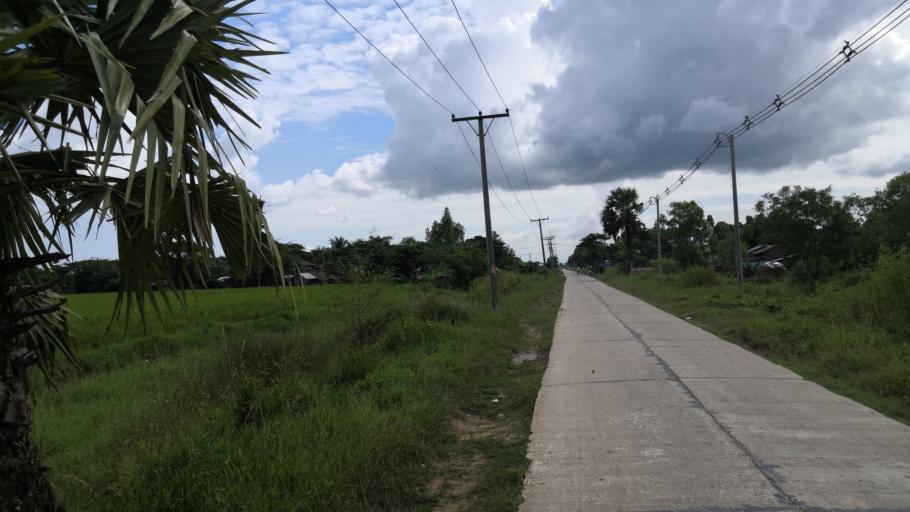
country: MM
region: Yangon
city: Kanbe
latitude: 16.4359
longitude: 96.1596
